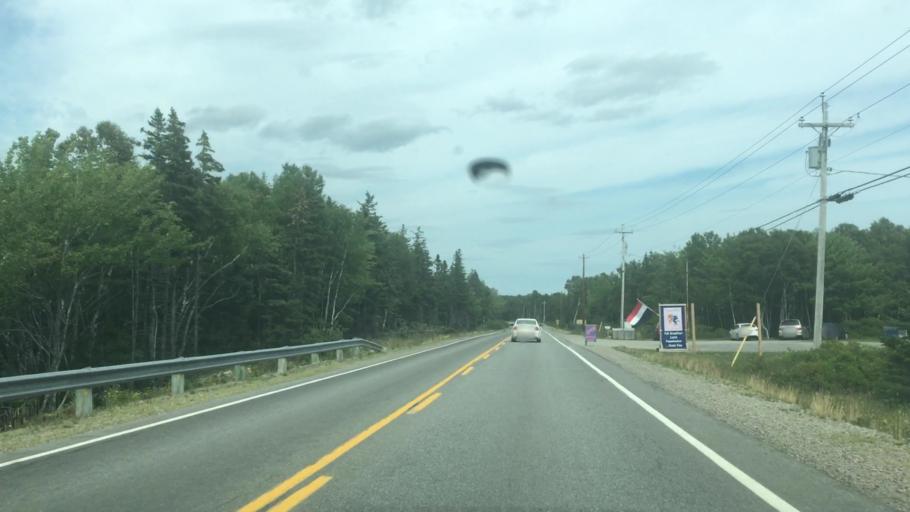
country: CA
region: Nova Scotia
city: Sydney Mines
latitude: 46.5061
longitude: -60.4336
